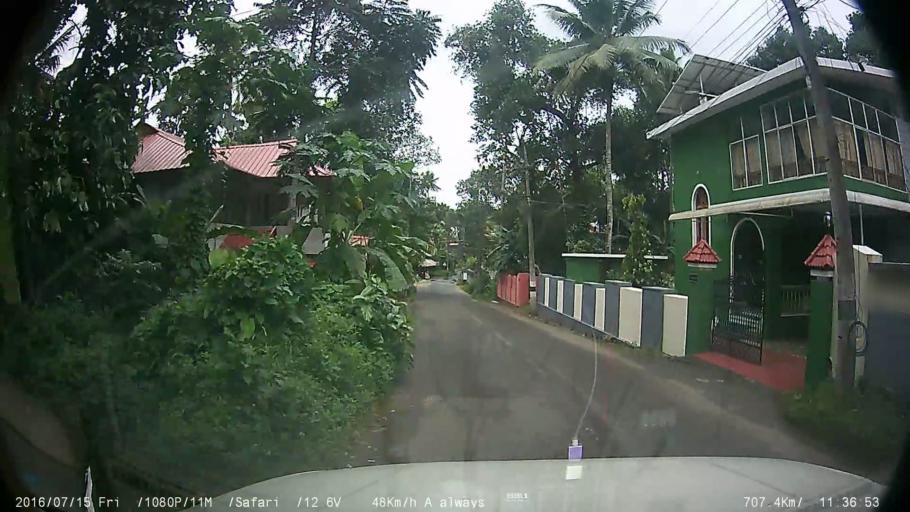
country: IN
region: Kerala
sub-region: Ernakulam
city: Piravam
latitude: 9.7715
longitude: 76.4929
